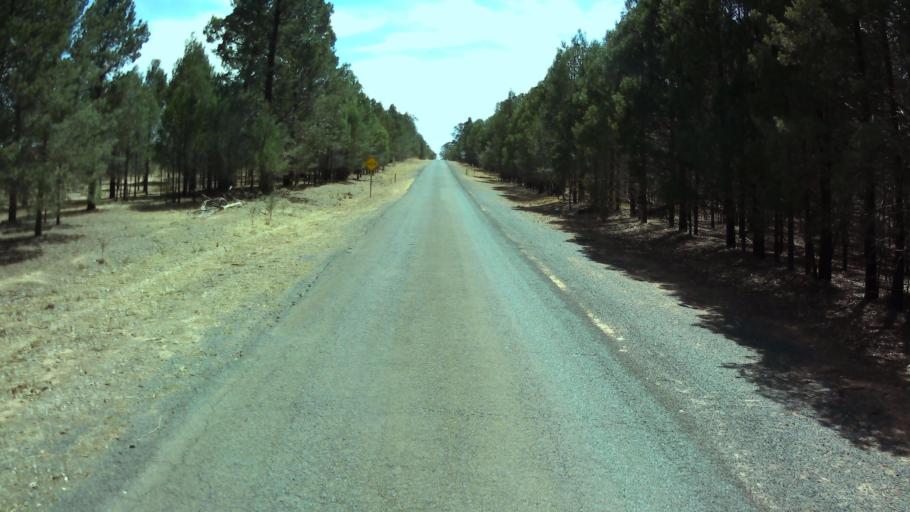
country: AU
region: New South Wales
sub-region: Weddin
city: Grenfell
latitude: -33.7618
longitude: 148.2050
